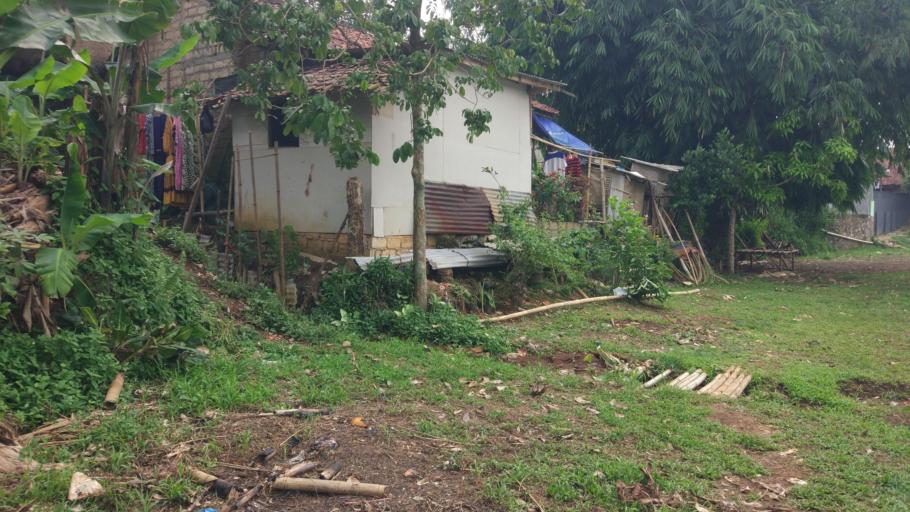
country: ID
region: West Java
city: Ciampea
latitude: -6.5750
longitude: 106.7293
